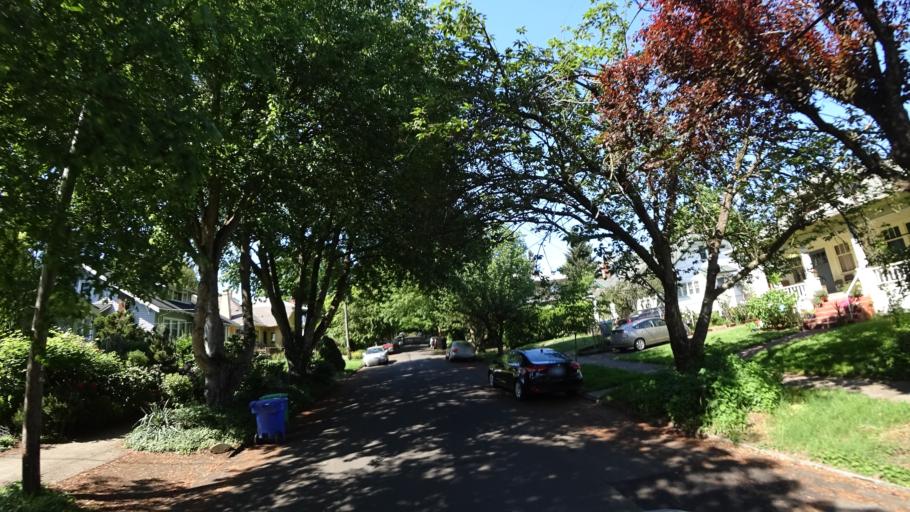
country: US
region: Oregon
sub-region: Multnomah County
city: Portland
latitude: 45.5398
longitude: -122.6535
